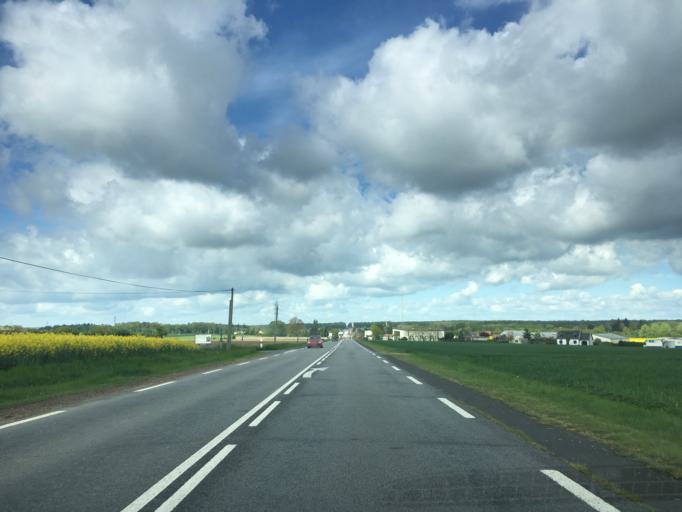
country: FR
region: Haute-Normandie
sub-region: Departement de l'Eure
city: Bourth
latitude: 48.7518
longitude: 0.7536
